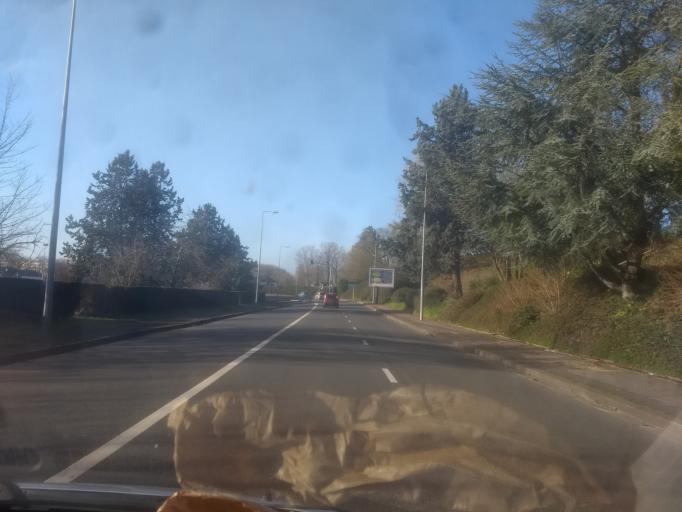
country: FR
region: Centre
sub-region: Departement du Cher
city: Bourges
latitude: 47.0952
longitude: 2.4025
